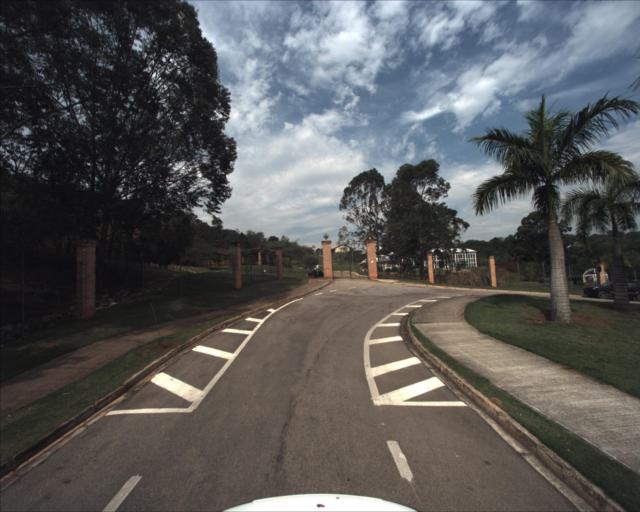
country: BR
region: Sao Paulo
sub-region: Sorocaba
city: Sorocaba
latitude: -23.4646
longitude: -47.4385
